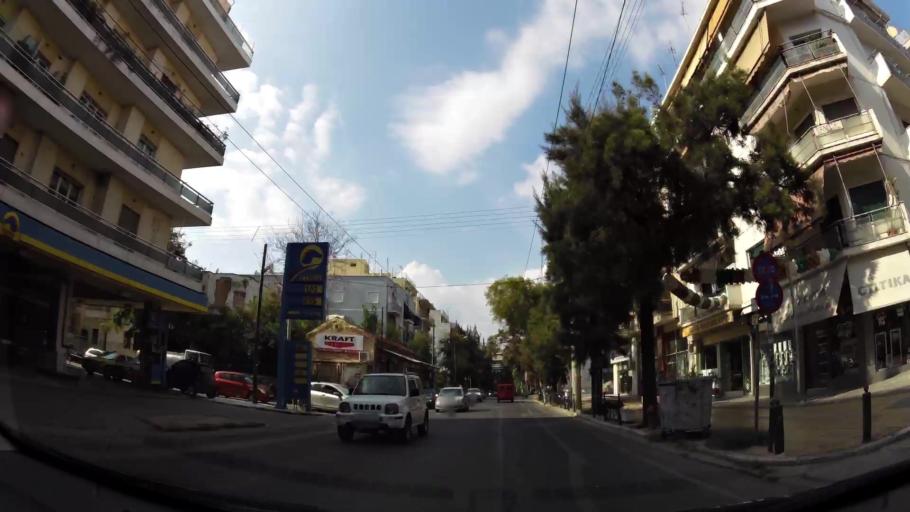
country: GR
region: Attica
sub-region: Nomarchia Athinas
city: Nea Chalkidona
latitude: 38.0238
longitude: 23.7349
